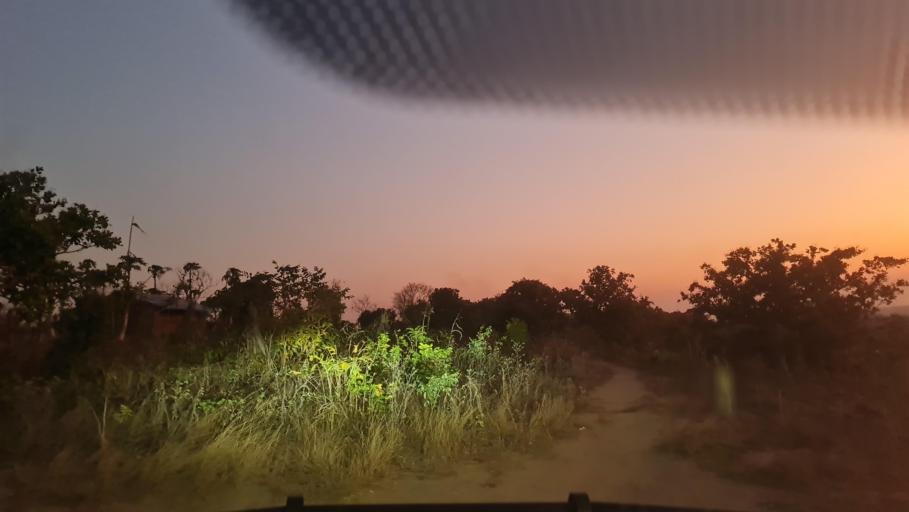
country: MZ
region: Nampula
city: Nacala
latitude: -14.0016
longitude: 40.0738
